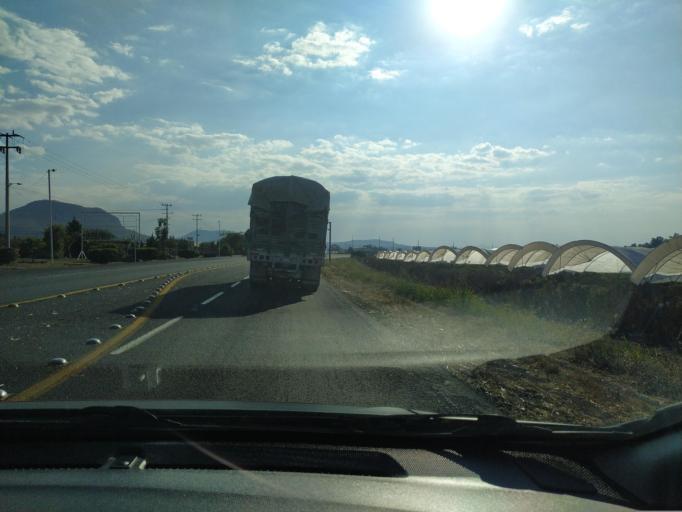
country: MX
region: Michoacan
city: Tanhuato de Guerrero
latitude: 20.2870
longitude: -102.3393
